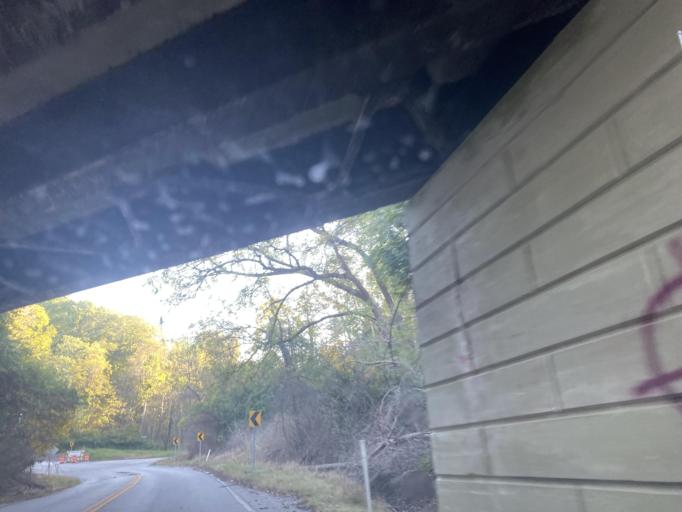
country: US
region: Kentucky
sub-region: Campbell County
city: Fort Thomas
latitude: 39.0983
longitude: -84.4399
